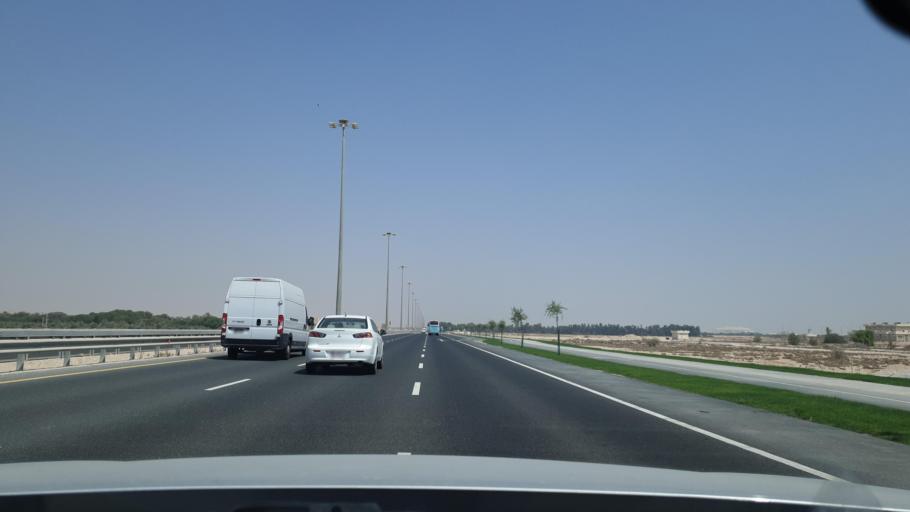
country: QA
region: Baladiyat az Za`ayin
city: Az Za`ayin
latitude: 25.6276
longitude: 51.4186
